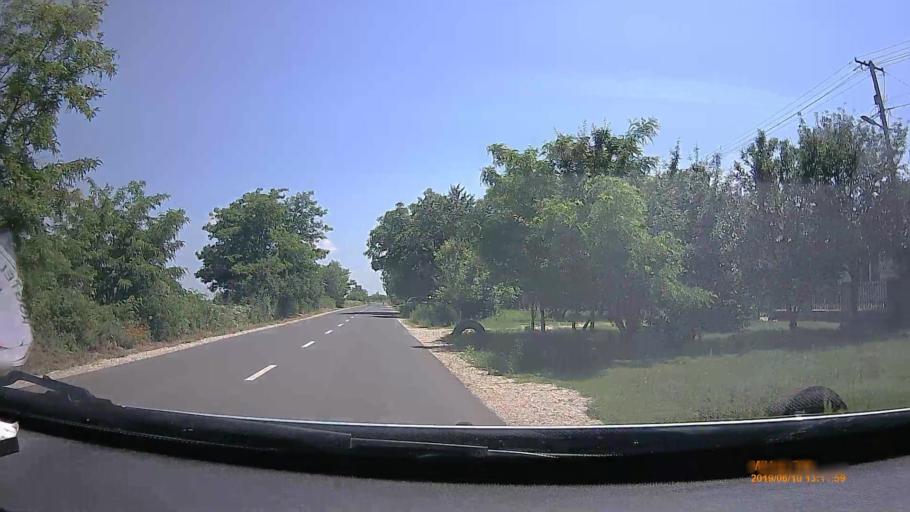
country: HU
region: Borsod-Abauj-Zemplen
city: Hernadnemeti
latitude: 48.0674
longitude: 20.9848
